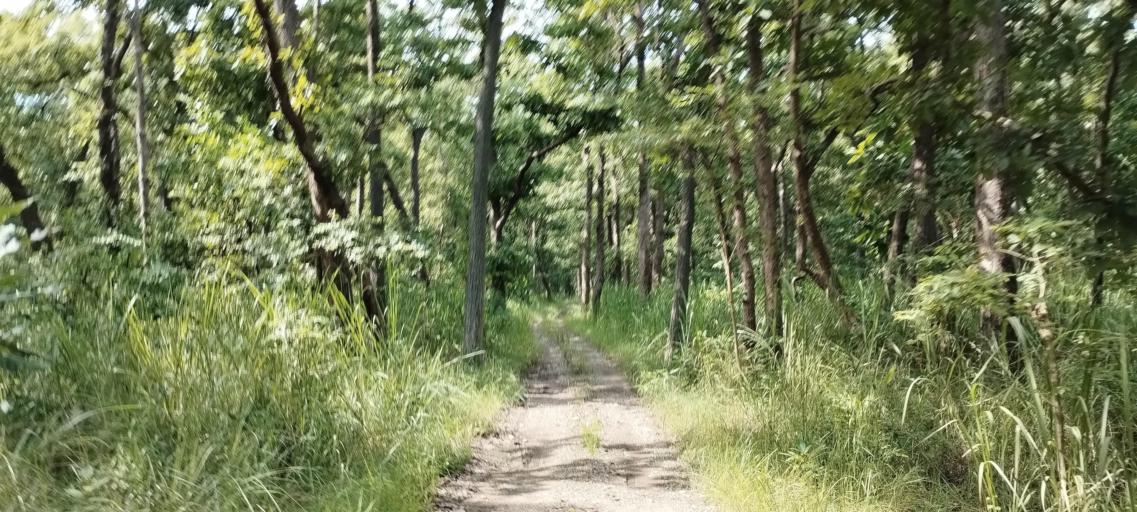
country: NP
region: Far Western
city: Tikapur
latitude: 28.5651
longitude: 81.2933
